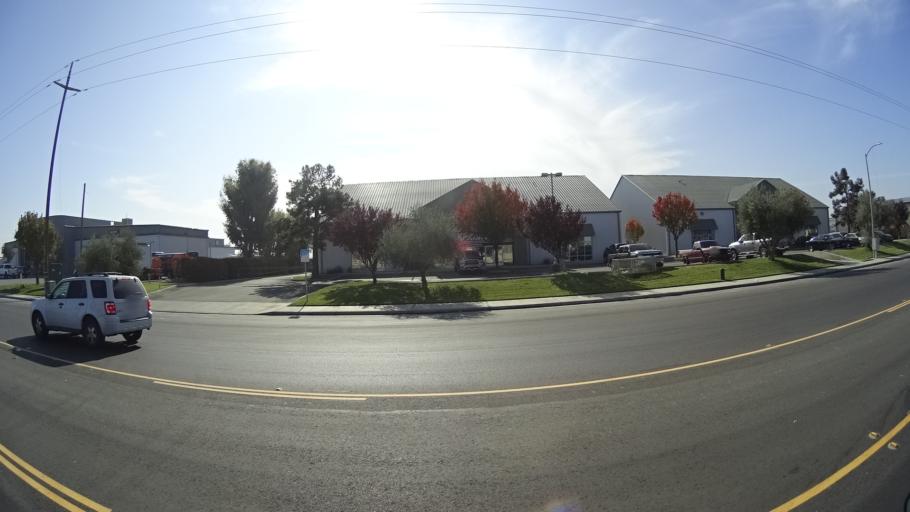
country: US
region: California
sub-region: Kern County
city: Bakersfield
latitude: 35.3542
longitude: -118.9545
